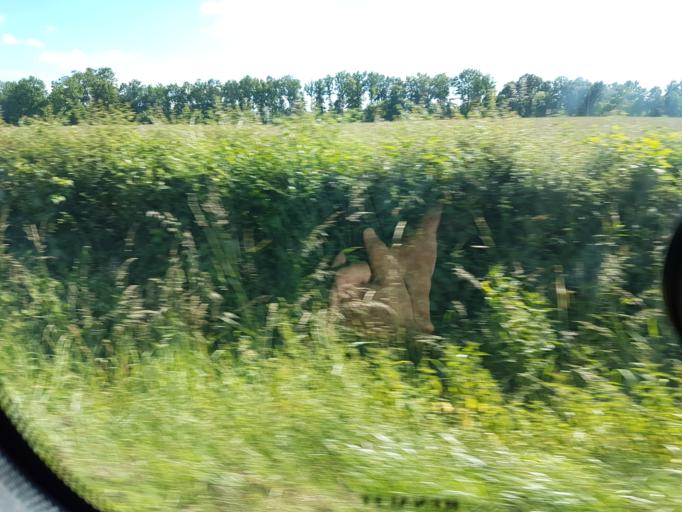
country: FR
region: Bourgogne
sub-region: Departement de Saone-et-Loire
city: Epinac
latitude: 47.0088
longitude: 4.4572
